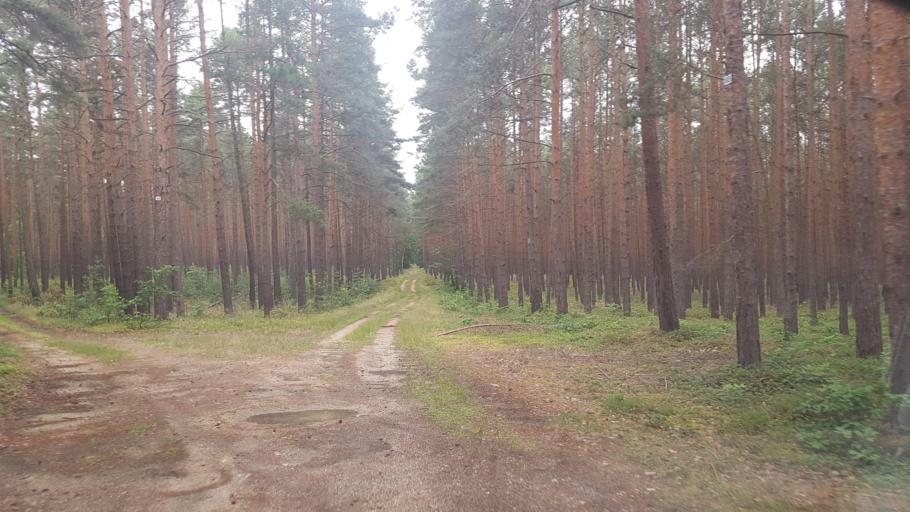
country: DE
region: Brandenburg
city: Crinitz
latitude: 51.7382
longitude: 13.7867
